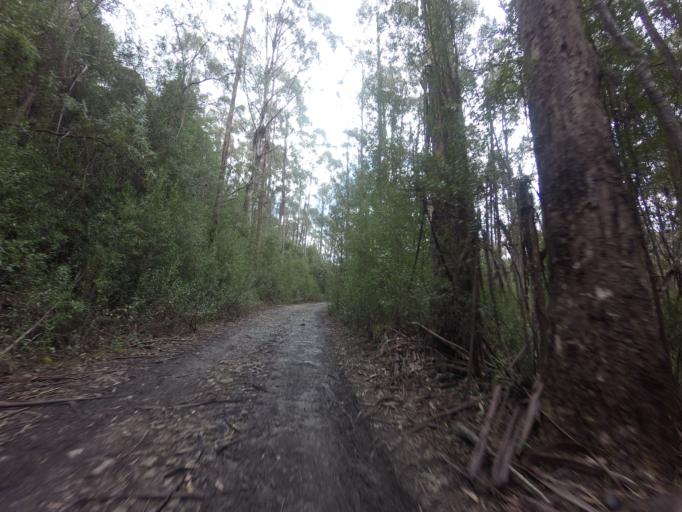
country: AU
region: Tasmania
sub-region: Huon Valley
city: Geeveston
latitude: -43.4034
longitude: 147.0088
